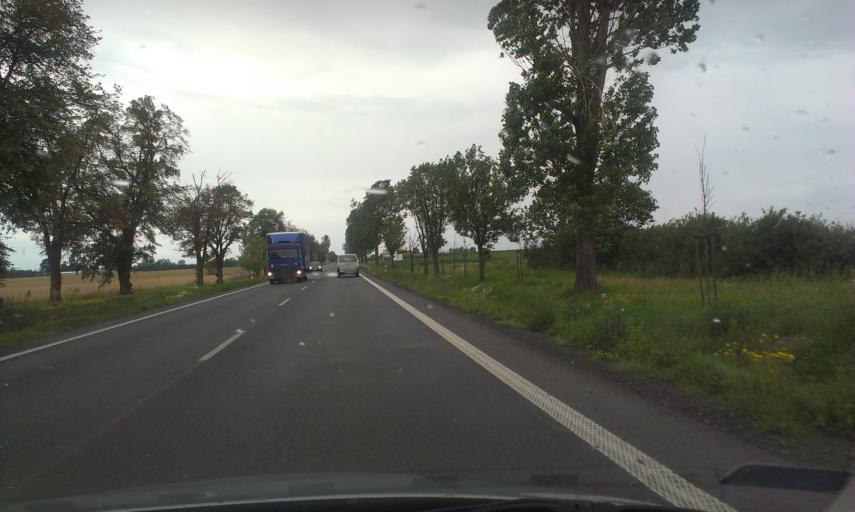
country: PL
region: Greater Poland Voivodeship
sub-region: Powiat obornicki
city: Oborniki
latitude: 52.6123
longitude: 16.8152
